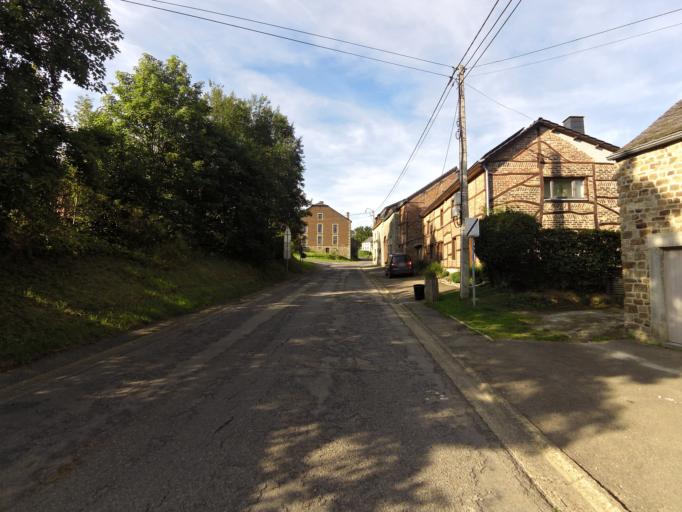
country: BE
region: Wallonia
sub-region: Province du Luxembourg
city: Erezee
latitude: 50.2649
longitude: 5.5583
